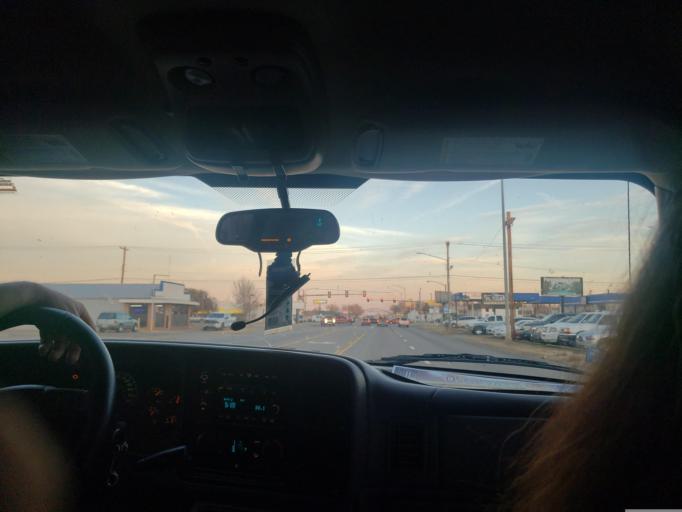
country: US
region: Kansas
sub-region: Seward County
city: Liberal
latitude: 37.0322
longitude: -100.9245
